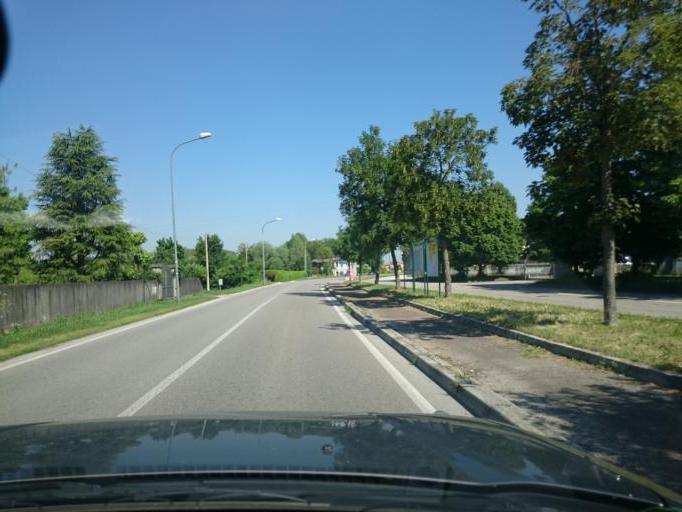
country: IT
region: Veneto
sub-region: Provincia di Venezia
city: Stra
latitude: 45.4214
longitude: 12.0144
